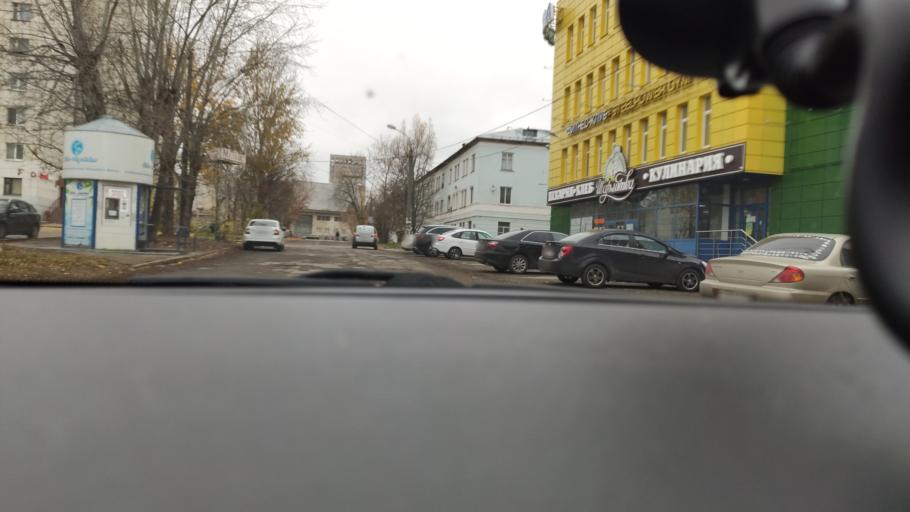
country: RU
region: Perm
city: Perm
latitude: 58.0222
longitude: 56.2994
